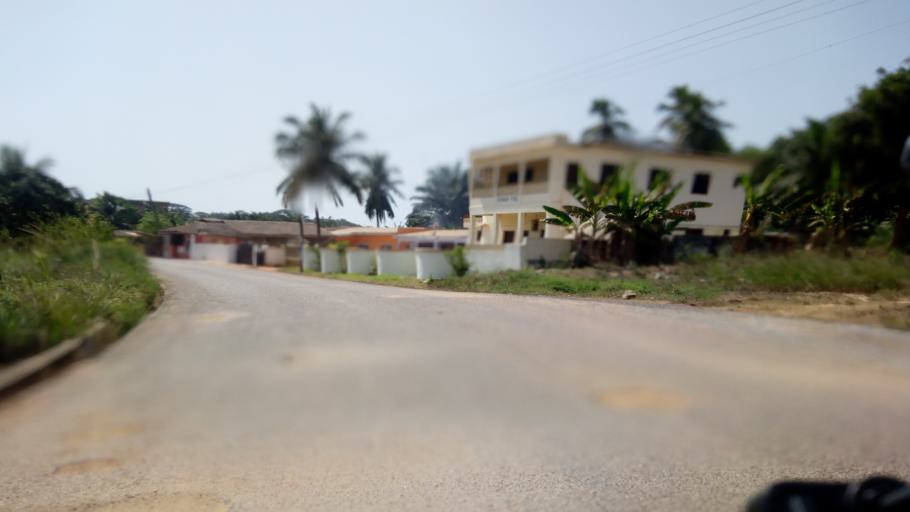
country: GH
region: Central
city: Cape Coast
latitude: 5.1108
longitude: -1.2723
